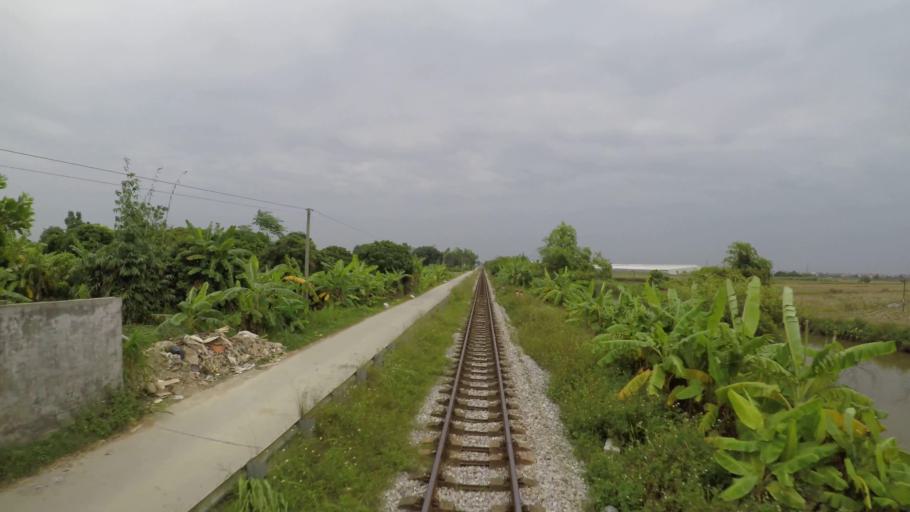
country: VN
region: Hai Duong
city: Lai Cach
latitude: 20.9528
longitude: 106.2293
